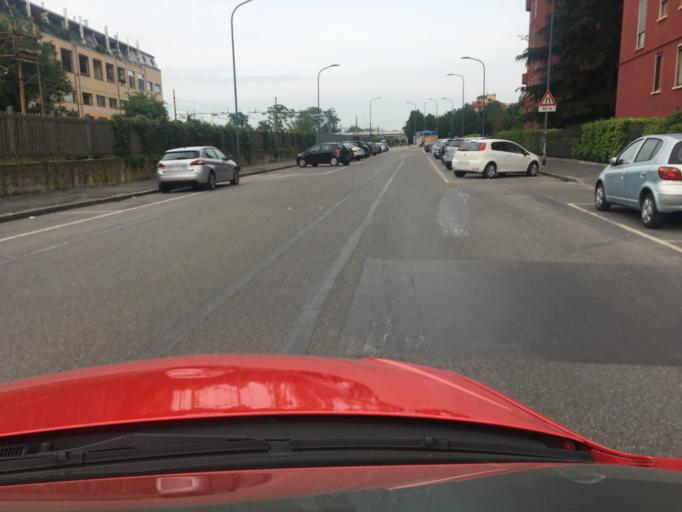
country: IT
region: Lombardy
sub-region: Citta metropolitana di Milano
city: Chiaravalle
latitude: 45.4460
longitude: 9.2200
